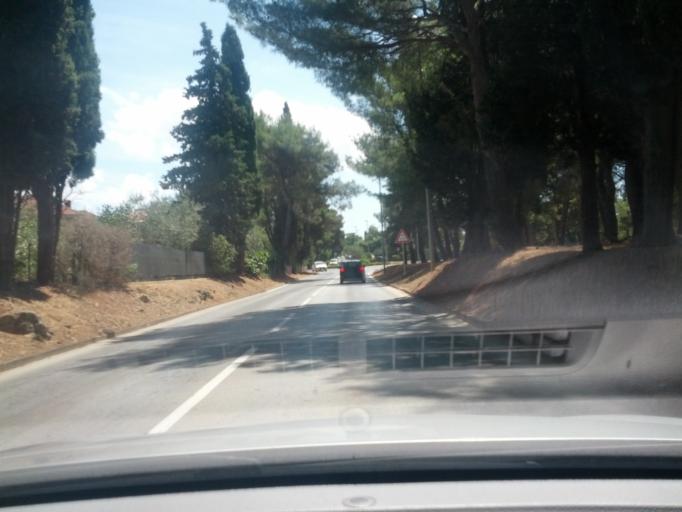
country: HR
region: Istarska
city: Fazana
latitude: 44.9165
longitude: 13.8138
